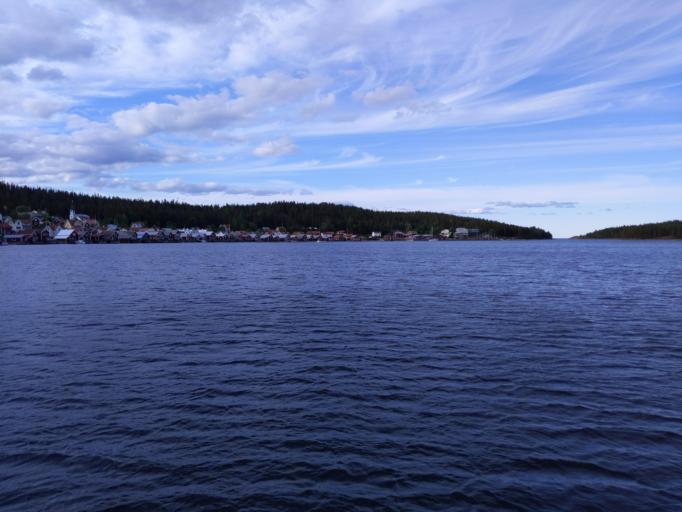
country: SE
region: Vaesternorrland
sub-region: OErnskoeldsviks Kommun
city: Kopmanholmen
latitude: 63.0178
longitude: 18.6462
